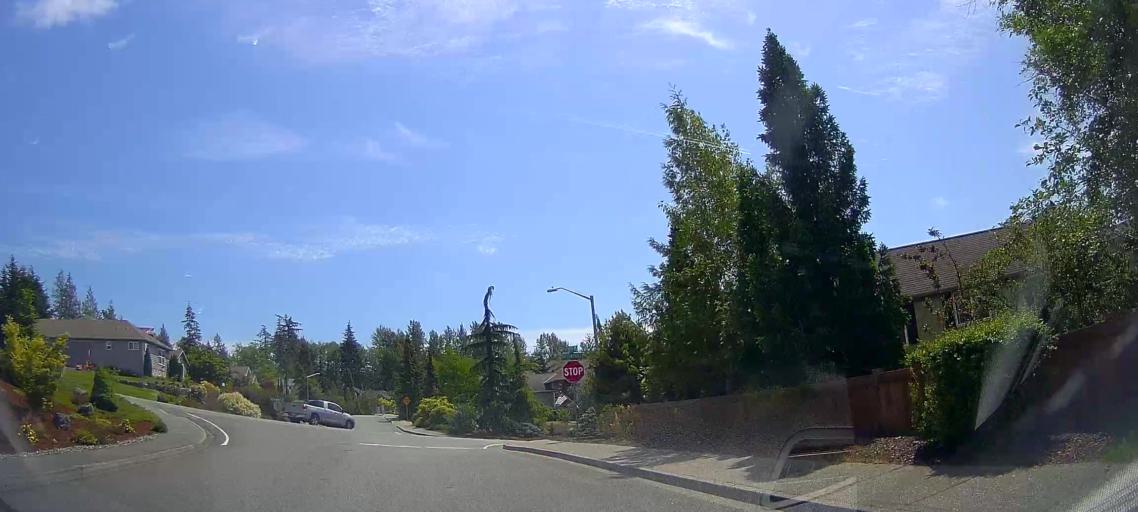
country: US
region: Washington
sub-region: Skagit County
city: Mount Vernon
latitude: 48.4164
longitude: -122.2909
